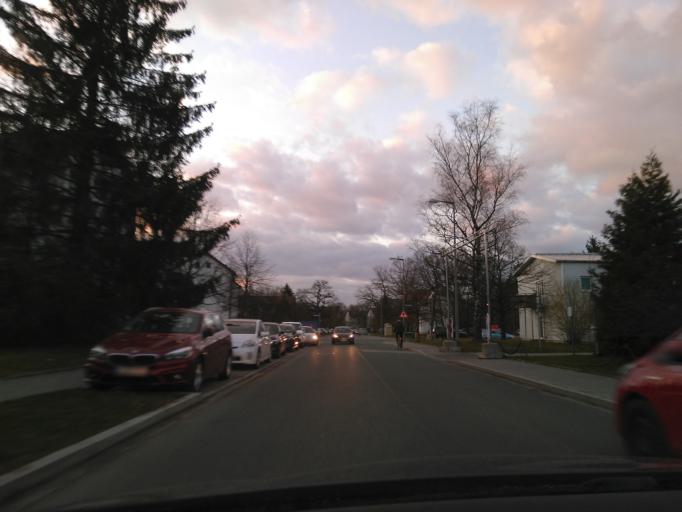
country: DE
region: Bavaria
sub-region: Upper Bavaria
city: Unterhaching
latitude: 48.0879
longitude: 11.5993
